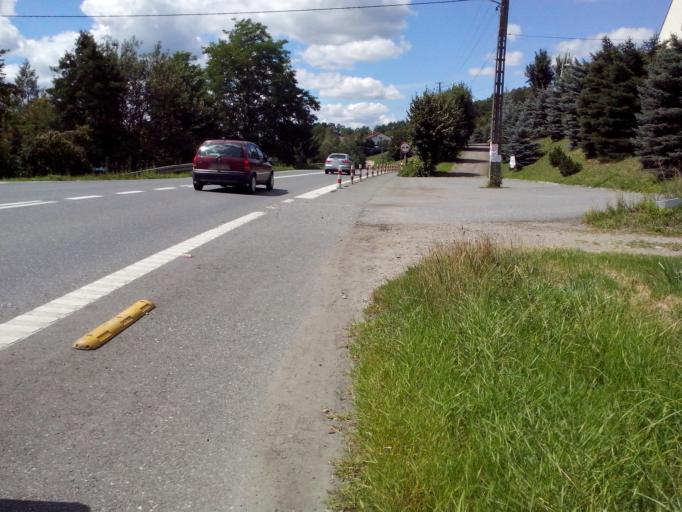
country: PL
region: Subcarpathian Voivodeship
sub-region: Powiat strzyzowski
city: Jawornik
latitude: 49.8049
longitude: 21.9026
